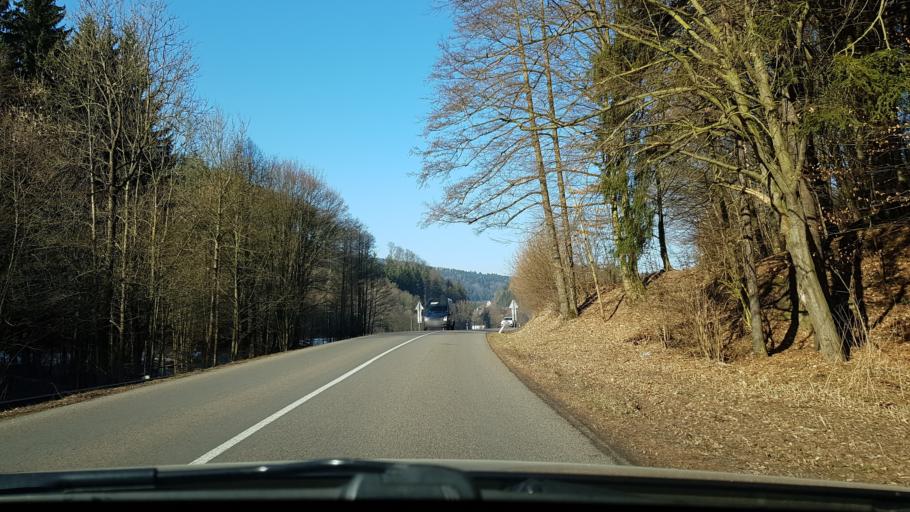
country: CZ
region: Olomoucky
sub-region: Okres Sumperk
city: Hanusovice
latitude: 50.0775
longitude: 16.9511
